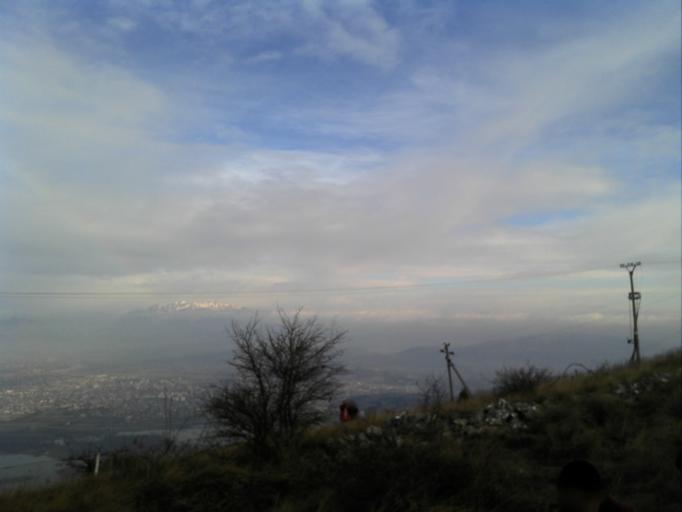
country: AL
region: Shkoder
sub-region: Rrethi i Shkodres
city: Berdica e Madhe
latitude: 42.0472
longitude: 19.4485
